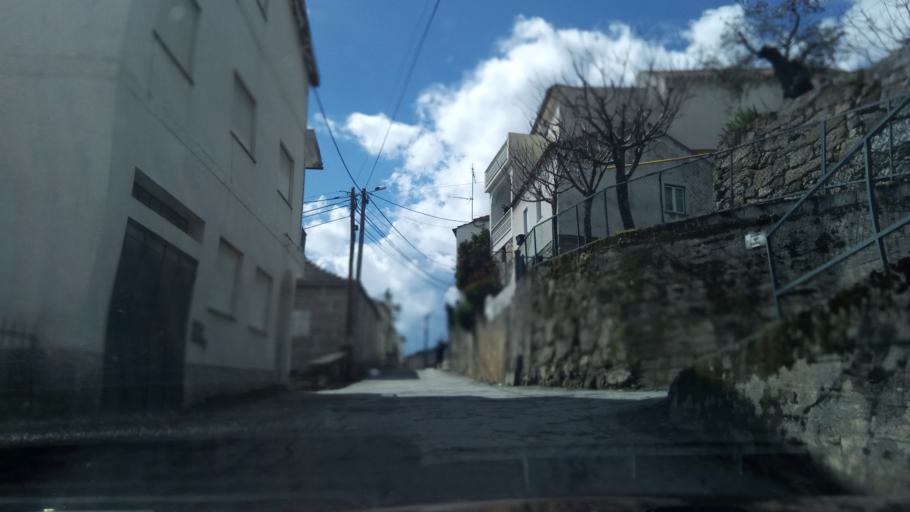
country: PT
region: Guarda
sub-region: Fornos de Algodres
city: Fornos de Algodres
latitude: 40.6637
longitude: -7.4926
